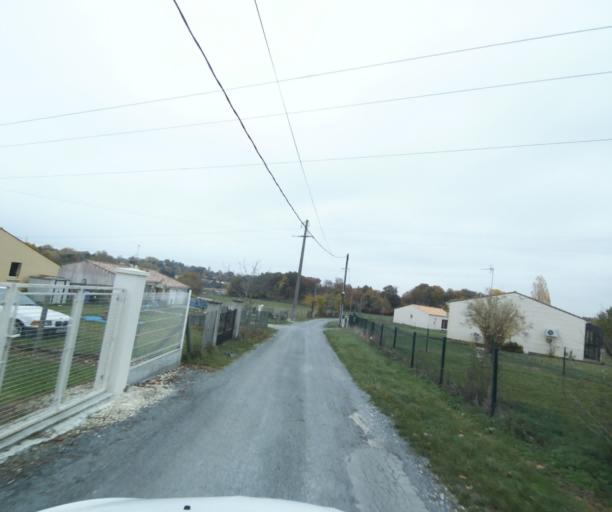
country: FR
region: Poitou-Charentes
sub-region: Departement de la Charente-Maritime
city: Les Gonds
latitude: 45.7369
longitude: -0.5994
